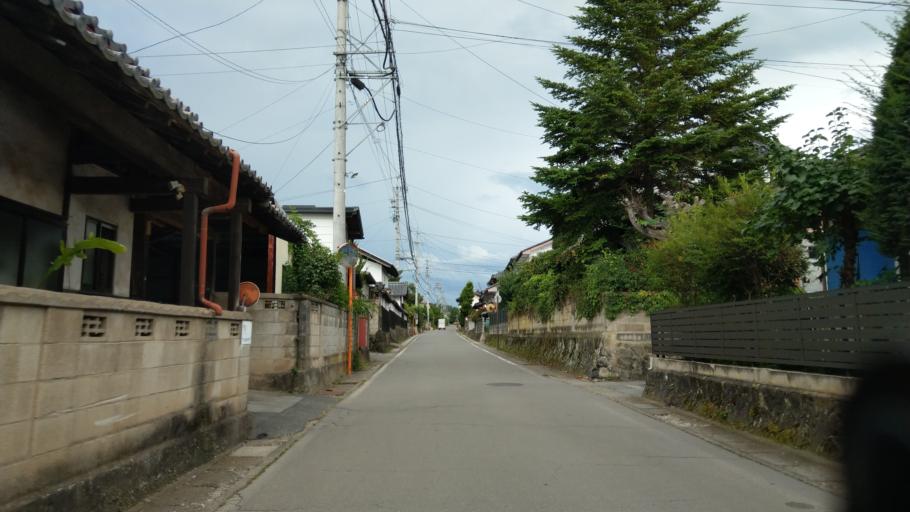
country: JP
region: Nagano
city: Komoro
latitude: 36.3127
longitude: 138.4656
